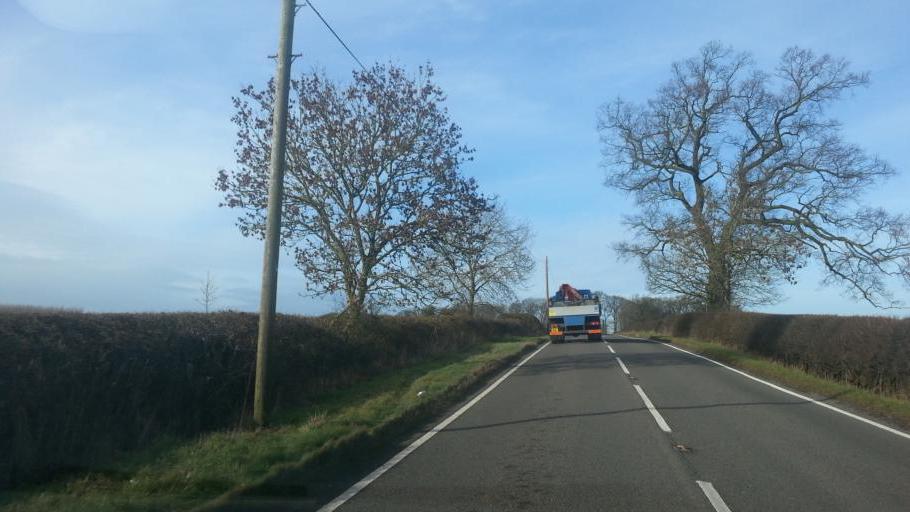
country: GB
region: England
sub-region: Leicestershire
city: Houghton on the Hill
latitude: 52.6692
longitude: -0.9318
